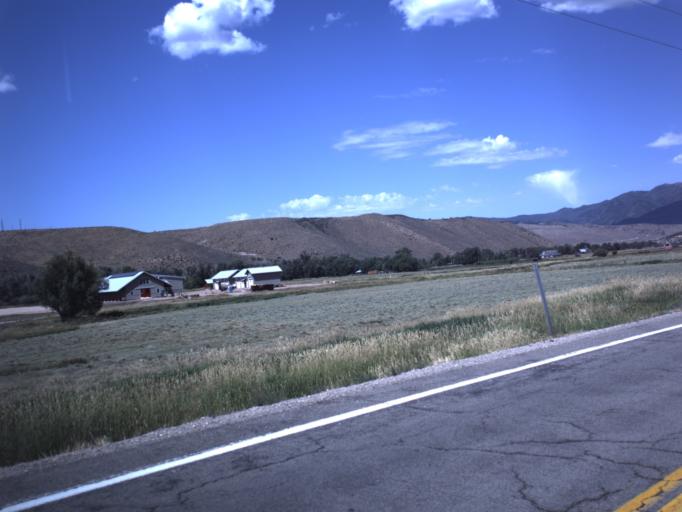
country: US
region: Utah
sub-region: Summit County
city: Oakley
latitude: 40.7331
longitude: -111.3488
